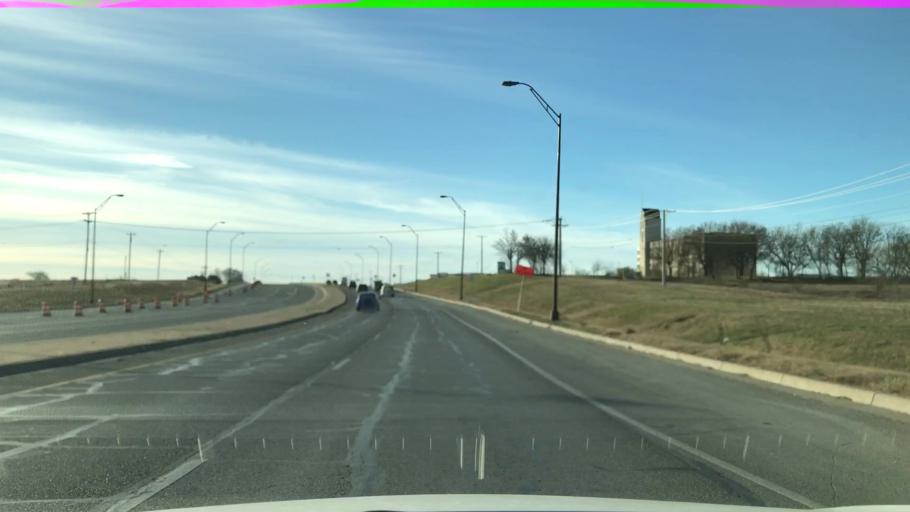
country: US
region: Texas
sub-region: Williamson County
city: Georgetown
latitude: 30.5720
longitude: -97.6505
